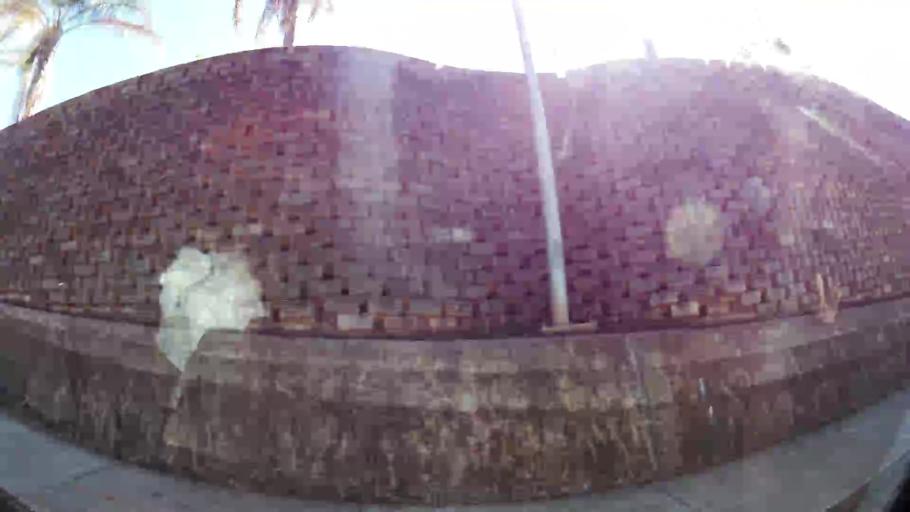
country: ZA
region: Limpopo
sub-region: Mopani District Municipality
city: Tzaneen
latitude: -23.8226
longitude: 30.1545
